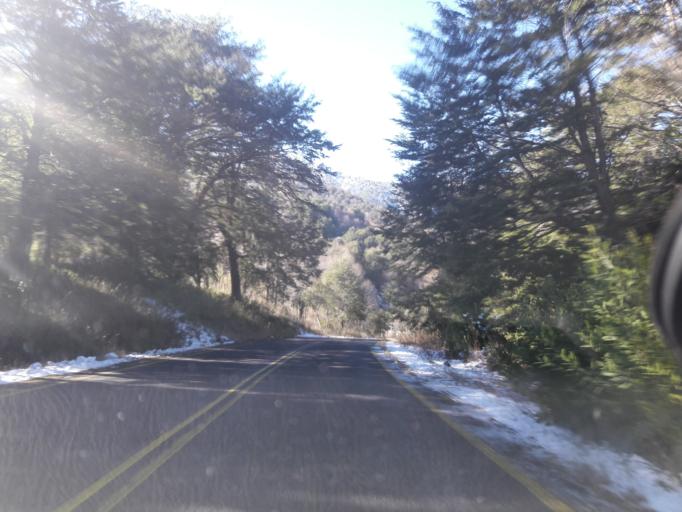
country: CL
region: Araucania
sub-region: Provincia de Cautin
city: Vilcun
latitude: -38.4614
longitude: -71.7145
